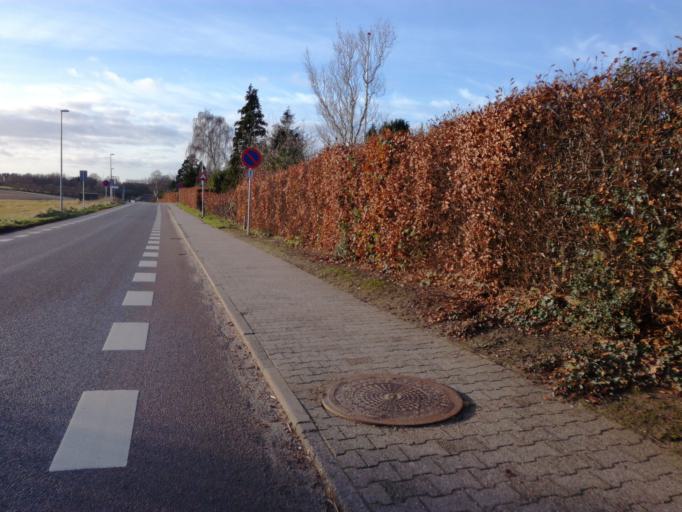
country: DK
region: South Denmark
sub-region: Fredericia Kommune
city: Fredericia
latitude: 55.6181
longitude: 9.7571
